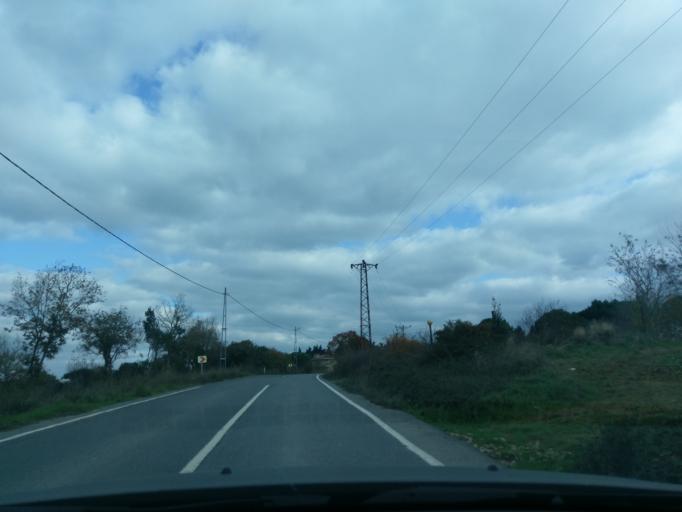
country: TR
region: Istanbul
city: Durusu
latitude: 41.3256
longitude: 28.6735
